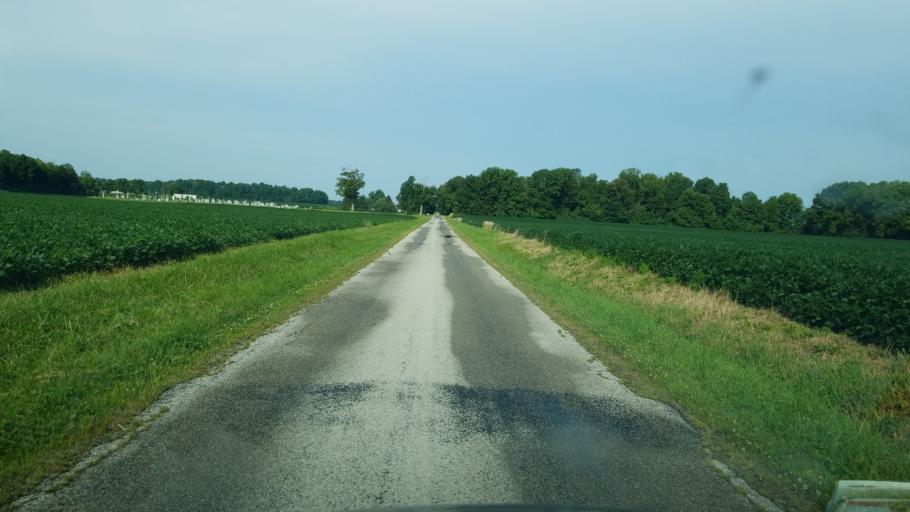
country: US
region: Ohio
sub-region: Crawford County
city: Crestline
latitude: 40.8213
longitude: -82.7823
